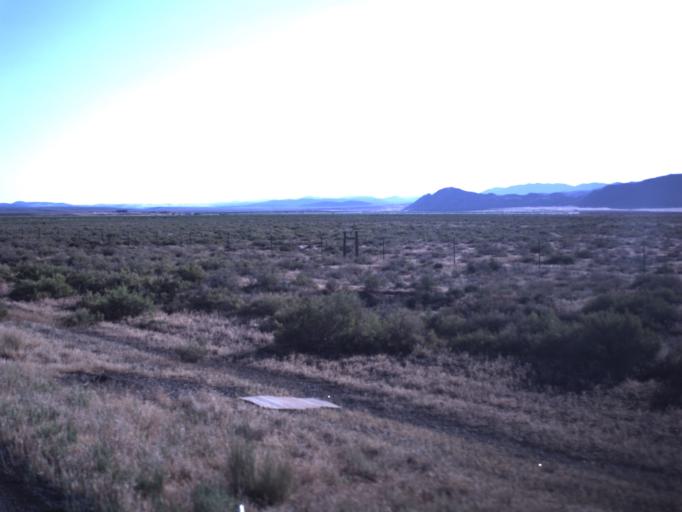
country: US
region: Utah
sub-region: Iron County
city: Enoch
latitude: 37.8712
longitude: -113.0316
